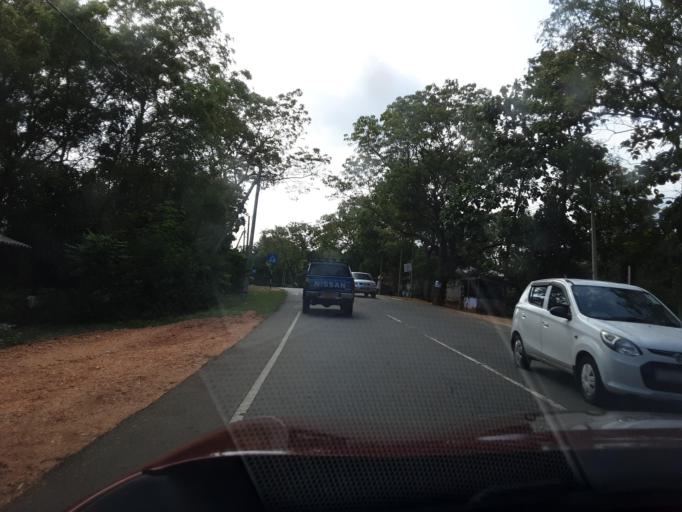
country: LK
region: Uva
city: Haputale
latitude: 6.3584
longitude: 81.1852
